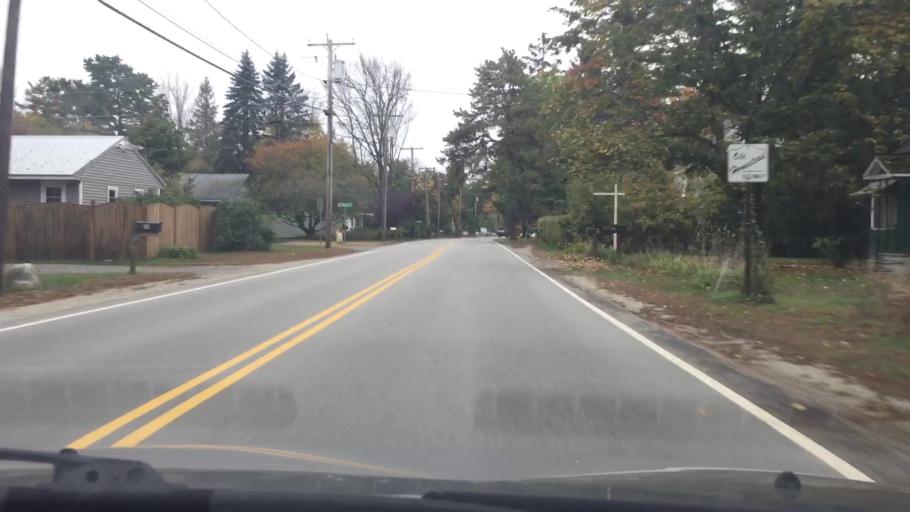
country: US
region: New Hampshire
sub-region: Cheshire County
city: Keene
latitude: 42.9086
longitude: -72.2652
